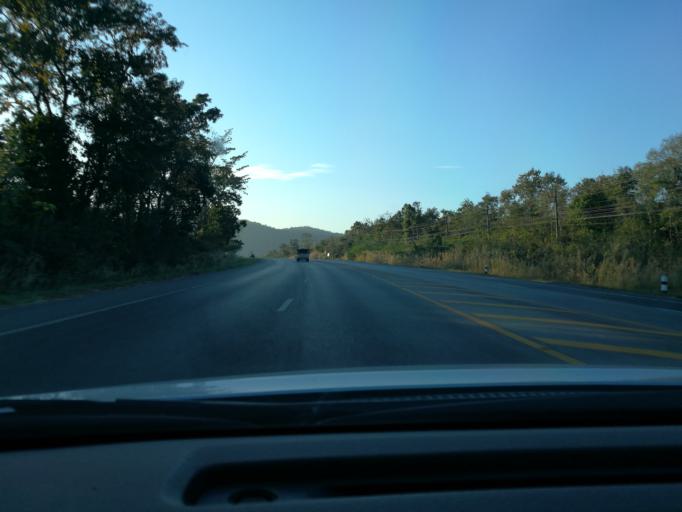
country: TH
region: Phitsanulok
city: Wang Thong
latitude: 16.8651
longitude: 100.4974
